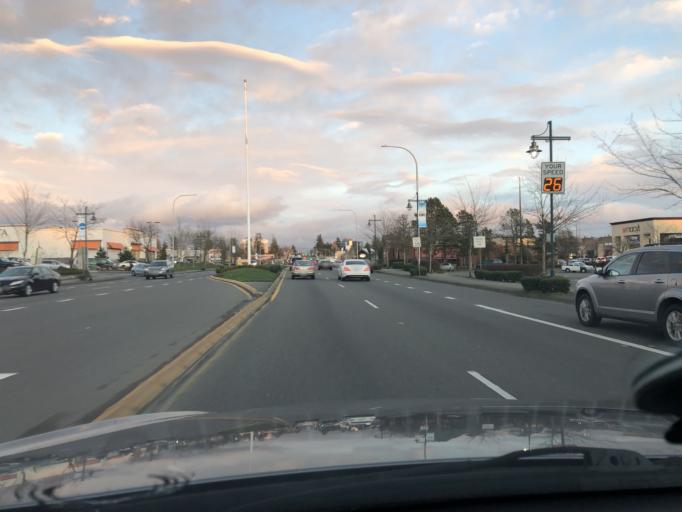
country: US
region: Washington
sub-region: King County
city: Federal Way
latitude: 47.3150
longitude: -122.3121
